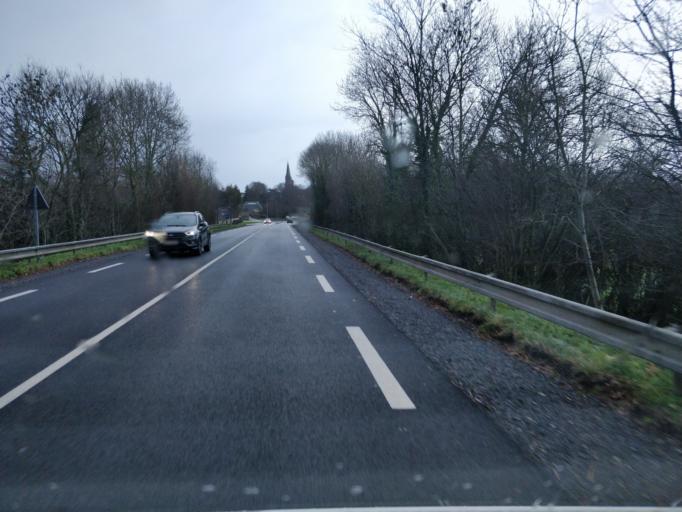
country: FR
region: Lower Normandy
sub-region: Departement du Calvados
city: Bayeux
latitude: 49.2684
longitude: -0.7088
